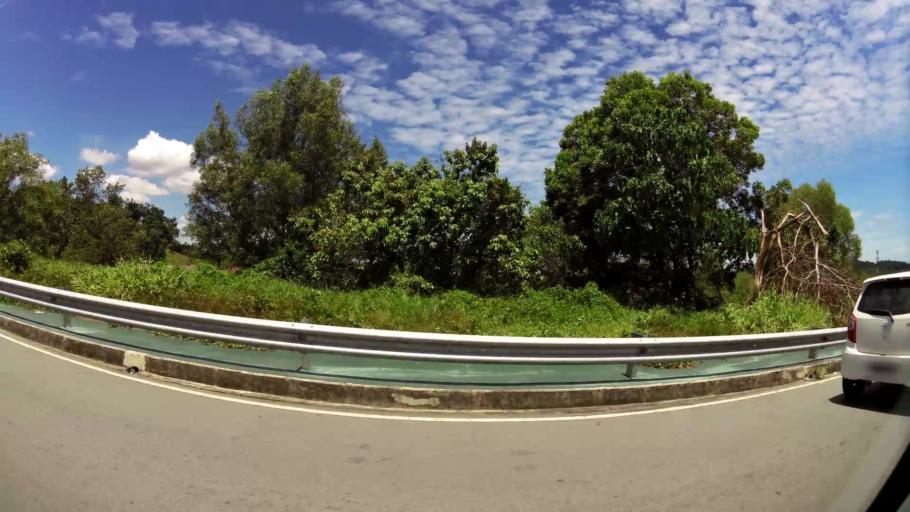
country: BN
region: Brunei and Muara
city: Bandar Seri Begawan
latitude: 5.0047
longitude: 115.0119
